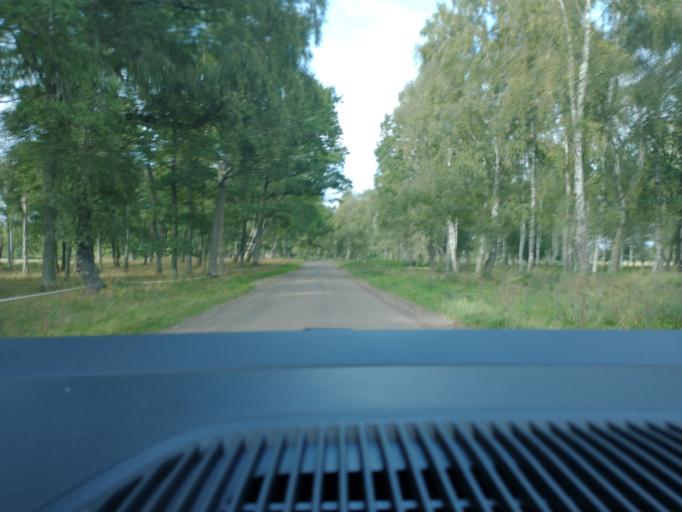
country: SE
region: Skane
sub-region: Lunds Kommun
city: Veberod
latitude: 55.6709
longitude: 13.4538
